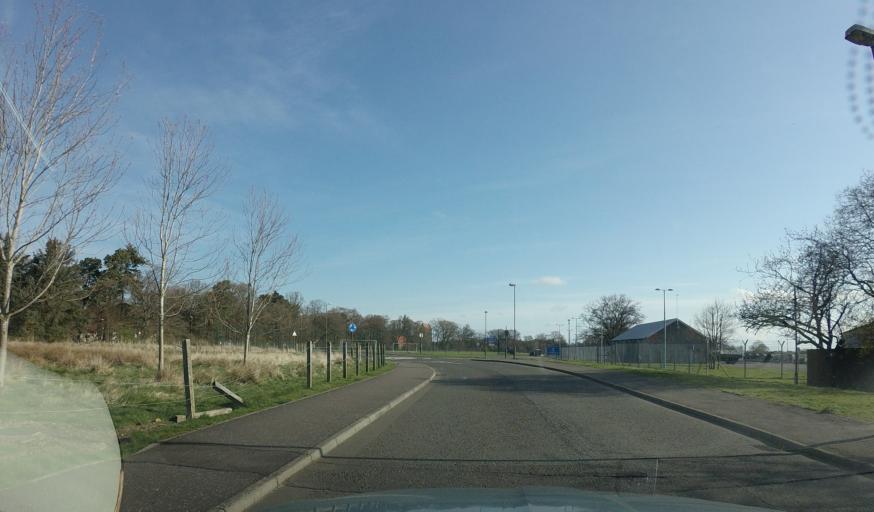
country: GB
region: Scotland
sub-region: Midlothian
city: Penicuik
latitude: 55.8479
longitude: -3.2063
